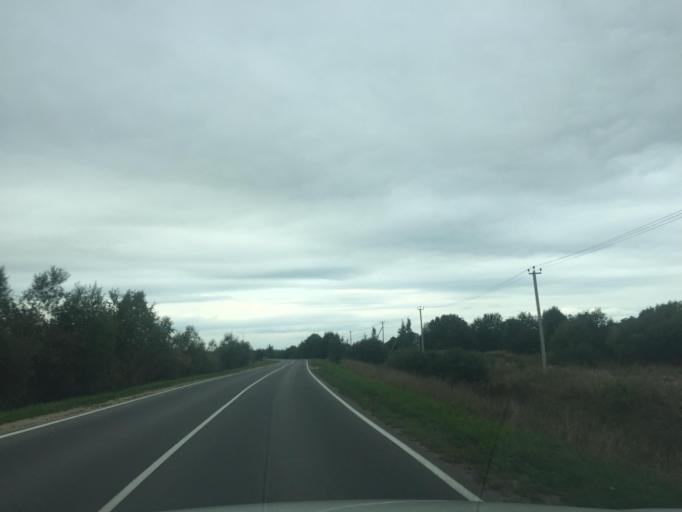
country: RU
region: Leningrad
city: Siverskiy
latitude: 59.3257
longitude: 30.0368
